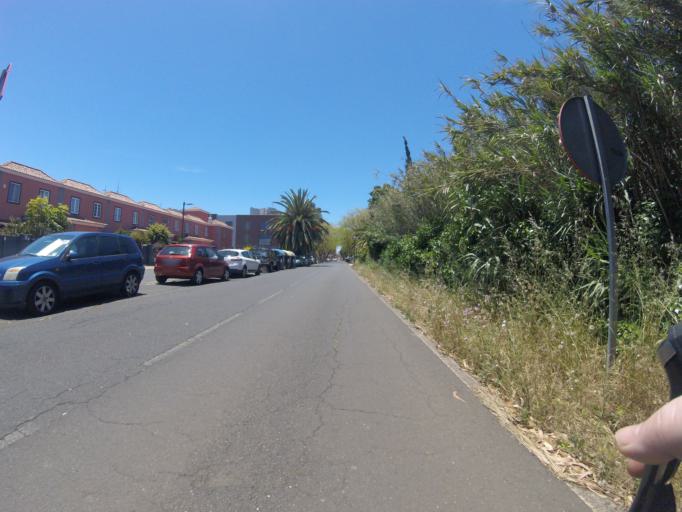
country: ES
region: Canary Islands
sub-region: Provincia de Santa Cruz de Tenerife
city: La Laguna
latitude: 28.4946
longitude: -16.3151
